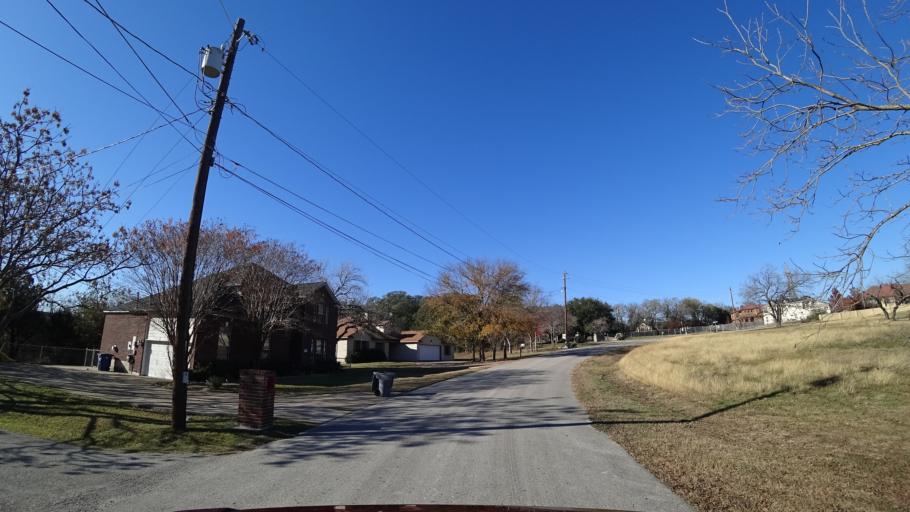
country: US
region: Texas
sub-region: Travis County
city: Wells Branch
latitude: 30.4047
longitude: -97.6945
